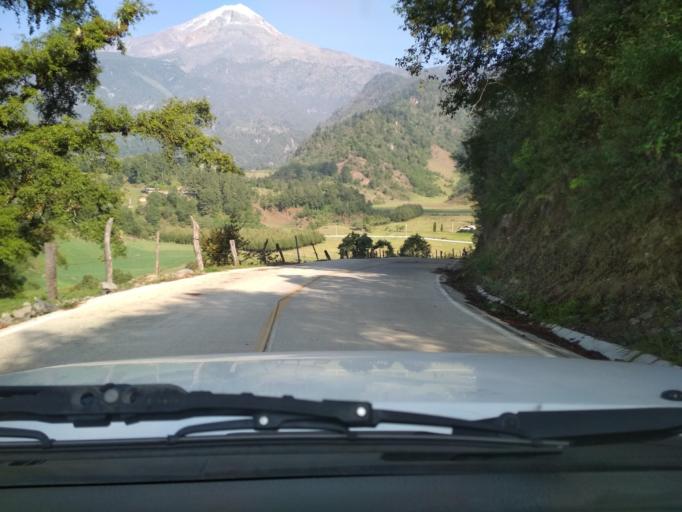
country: MX
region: Veracruz
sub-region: La Perla
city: Chilapa
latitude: 19.0033
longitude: -97.1783
